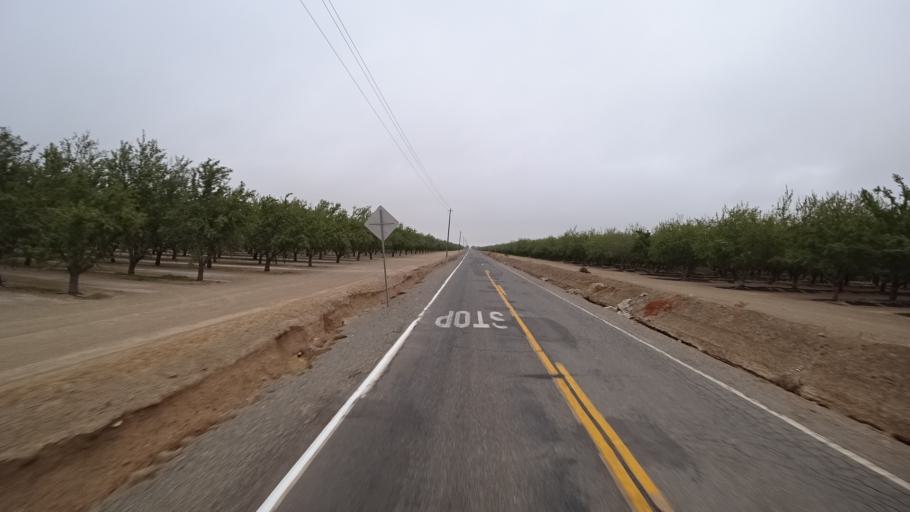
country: US
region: California
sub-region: Colusa County
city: Arbuckle
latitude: 38.9259
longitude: -122.0599
